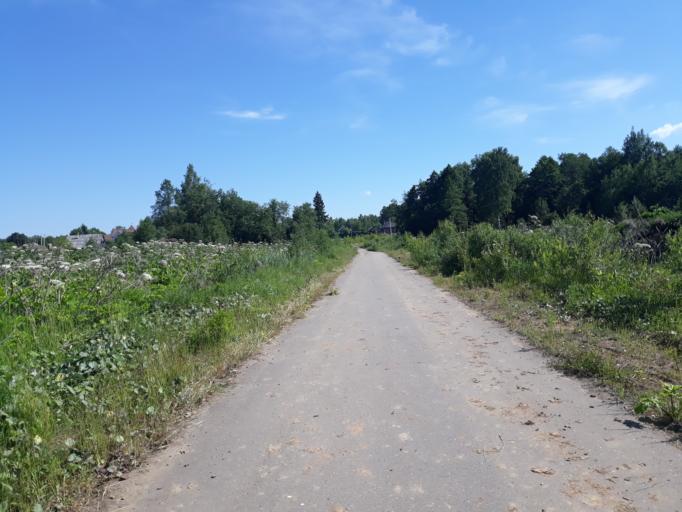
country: RU
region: Ivanovo
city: Novo-Talitsy
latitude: 57.0649
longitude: 40.6987
